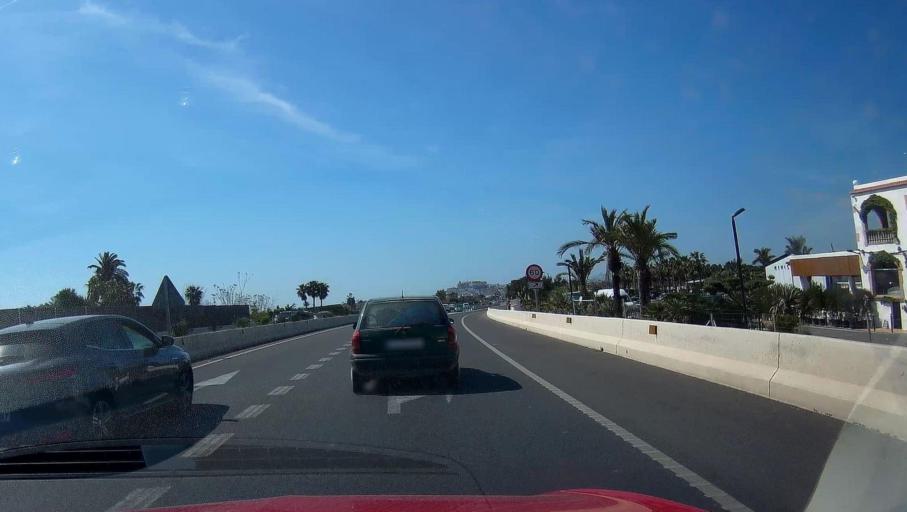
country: ES
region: Balearic Islands
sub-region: Illes Balears
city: Ibiza
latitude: 38.9341
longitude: 1.4442
